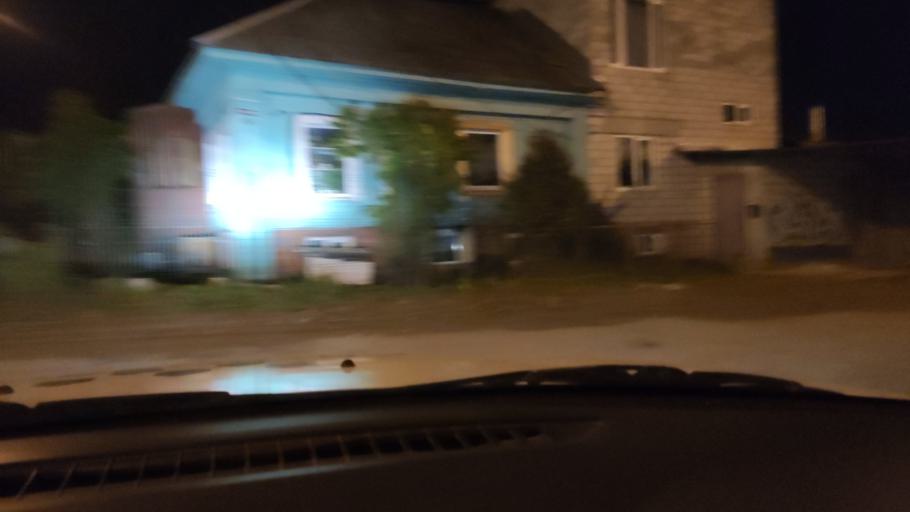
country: RU
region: Perm
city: Kondratovo
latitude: 57.9632
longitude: 56.1503
